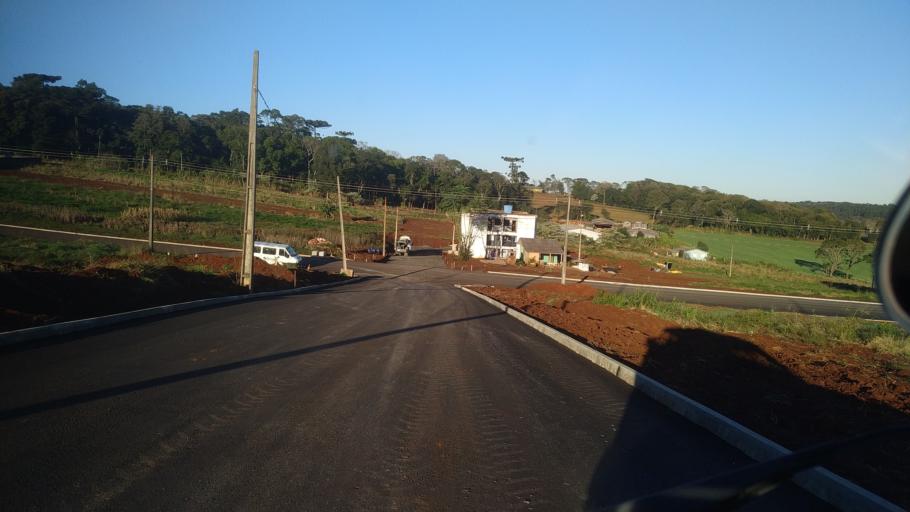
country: BR
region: Santa Catarina
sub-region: Chapeco
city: Chapeco
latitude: -27.0887
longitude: -52.6943
